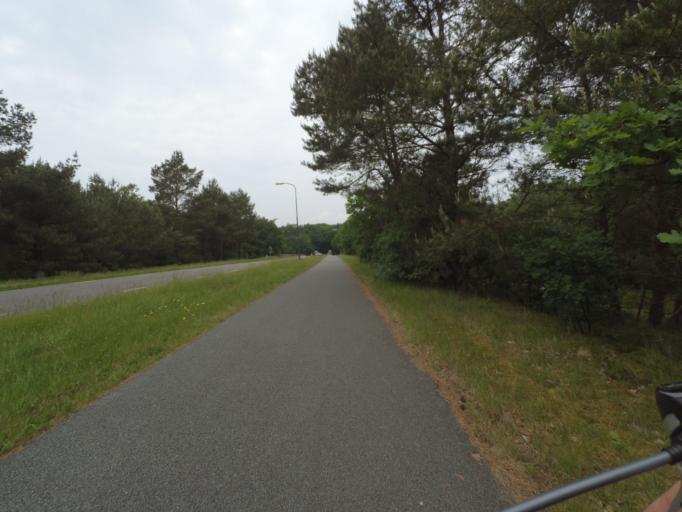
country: NL
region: Gelderland
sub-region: Gemeente Renkum
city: Wolfheze
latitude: 51.9979
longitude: 5.7986
